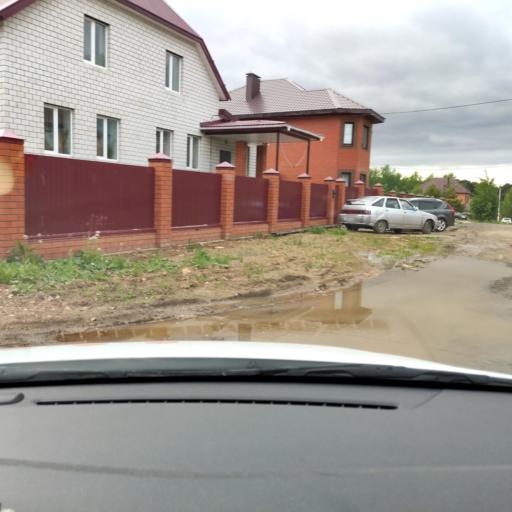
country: RU
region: Tatarstan
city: Vysokaya Gora
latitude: 55.7845
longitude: 49.2605
